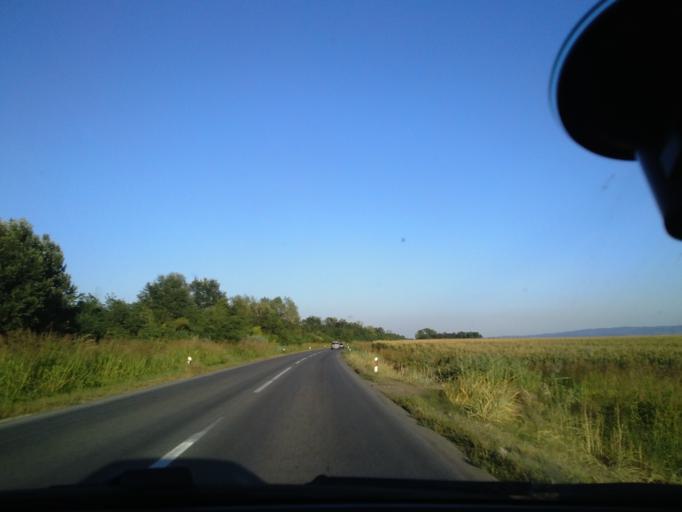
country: RS
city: Kisac
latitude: 45.3329
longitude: 19.6807
